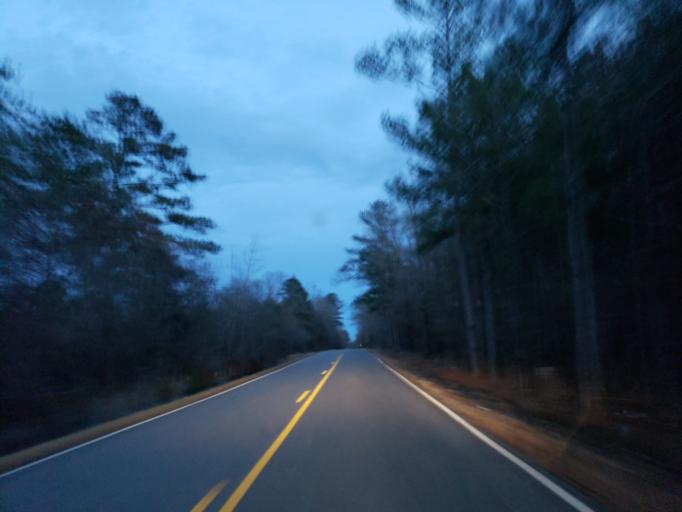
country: US
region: Alabama
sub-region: Greene County
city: Eutaw
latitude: 32.8858
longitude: -88.0531
